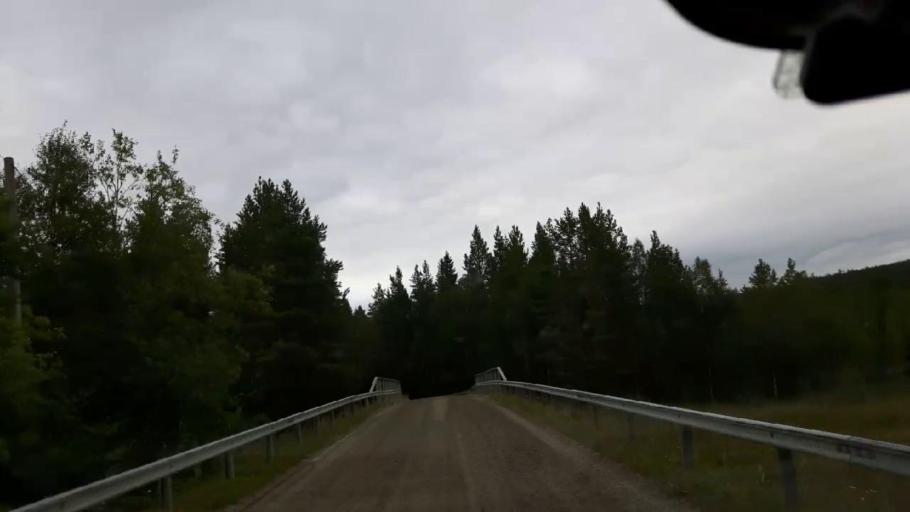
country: SE
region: Jaemtland
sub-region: Braecke Kommun
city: Braecke
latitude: 62.9233
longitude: 15.5431
